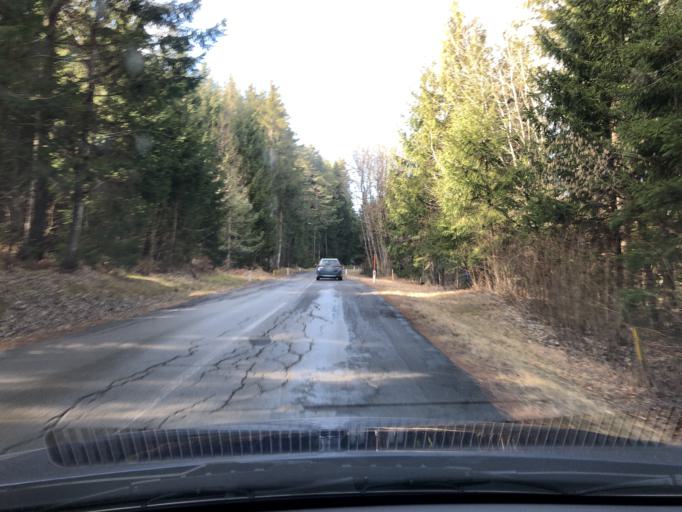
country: AT
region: Carinthia
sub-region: Politischer Bezirk Villach Land
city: Paternion
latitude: 46.7048
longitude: 13.6307
